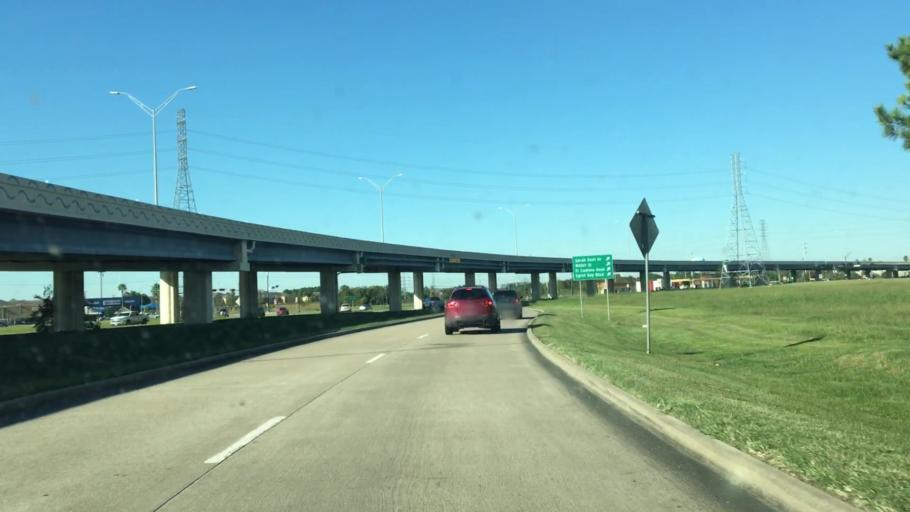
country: US
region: Texas
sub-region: Harris County
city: Webster
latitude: 29.5394
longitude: -95.1119
